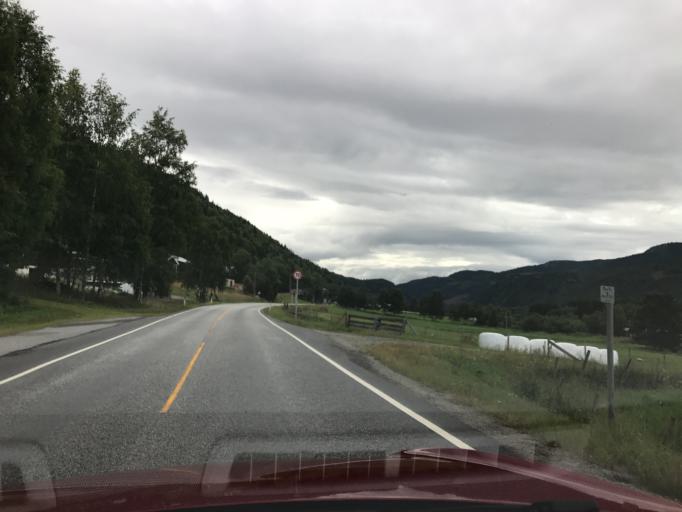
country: NO
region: Buskerud
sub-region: Nore og Uvdal
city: Rodberg
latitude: 60.2609
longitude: 8.8435
